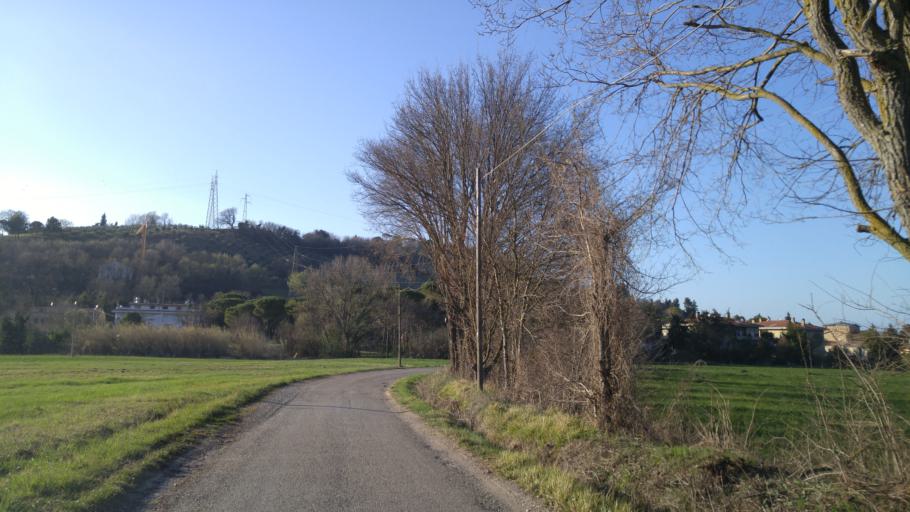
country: IT
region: The Marches
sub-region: Provincia di Pesaro e Urbino
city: Pesaro
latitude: 43.8794
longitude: 12.9021
